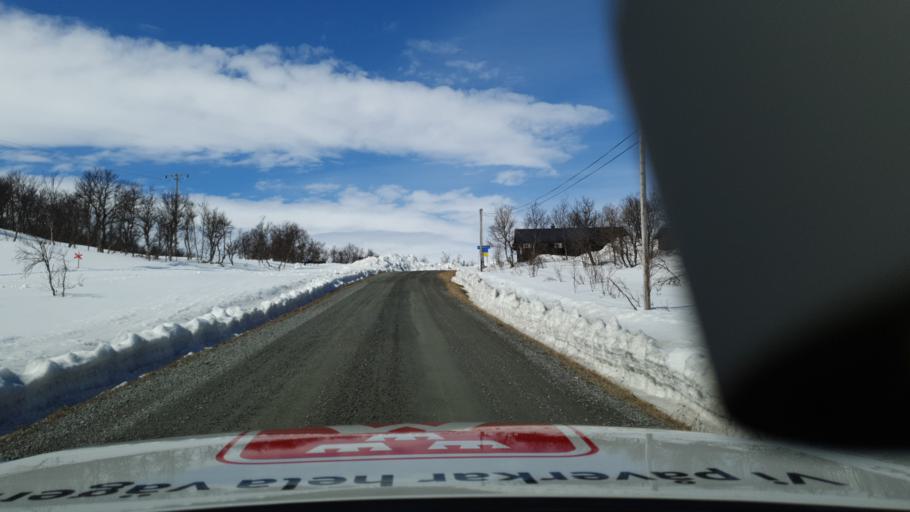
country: SE
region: Jaemtland
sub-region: Are Kommun
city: Are
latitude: 62.8947
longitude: 12.7114
